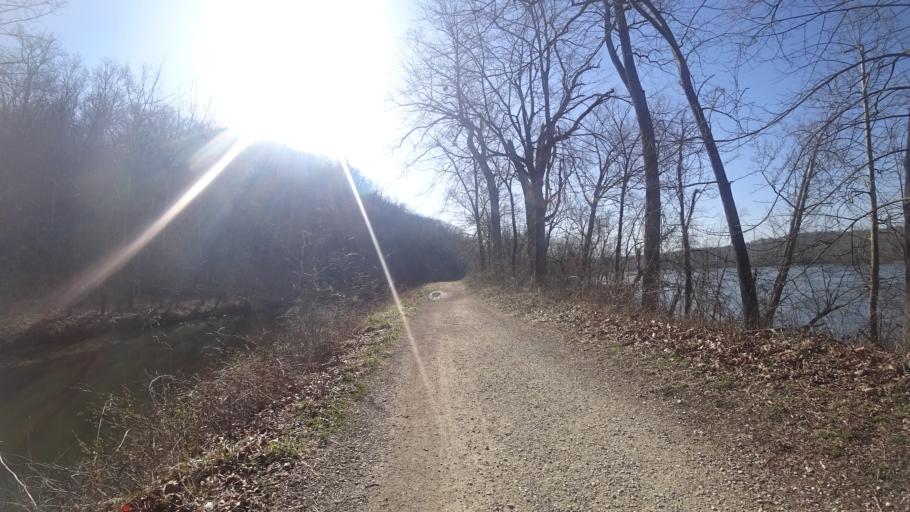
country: US
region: Virginia
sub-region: Loudoun County
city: Lowes Island
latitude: 39.0633
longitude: -77.3196
